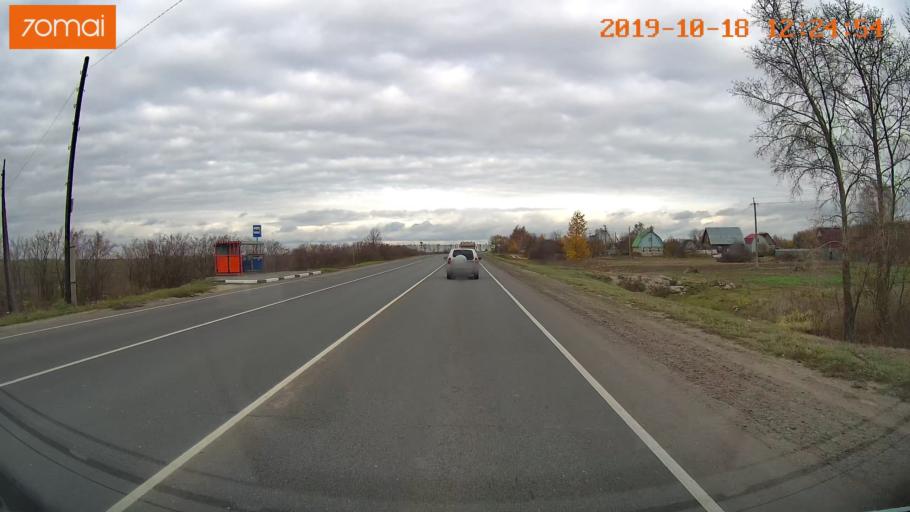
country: RU
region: Rjazan
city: Rybnoye
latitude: 54.5439
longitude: 39.5158
